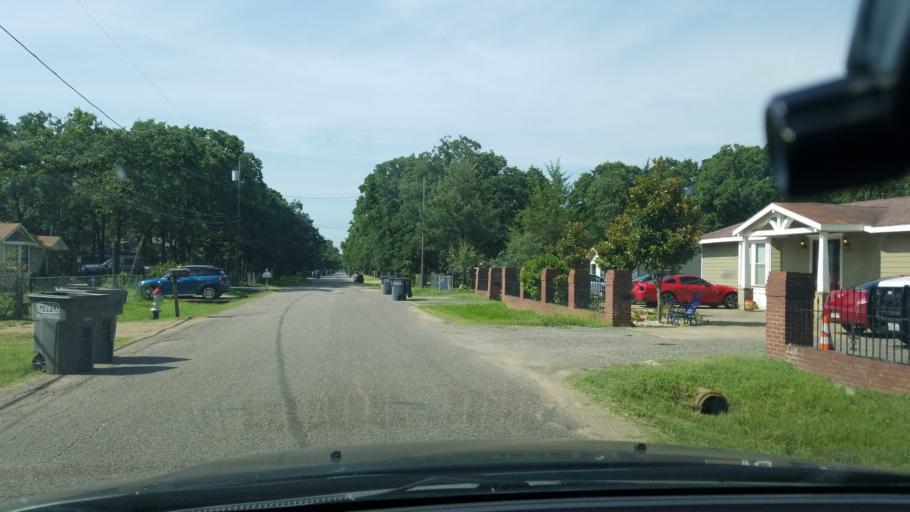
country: US
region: Texas
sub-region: Dallas County
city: Balch Springs
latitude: 32.7182
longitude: -96.6346
